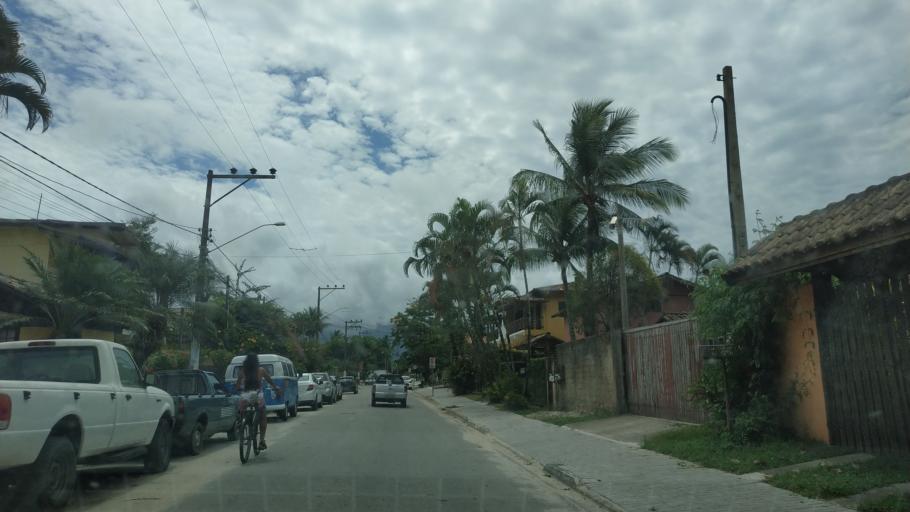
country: BR
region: Sao Paulo
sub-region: Ilhabela
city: Ilhabela
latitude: -23.8217
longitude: -45.3679
